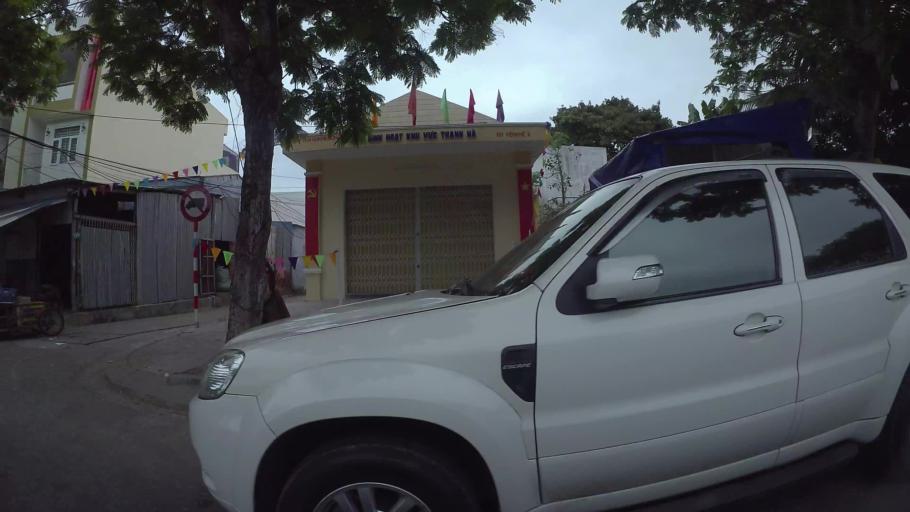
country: VN
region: Da Nang
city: Thanh Khe
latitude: 16.0718
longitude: 108.1820
